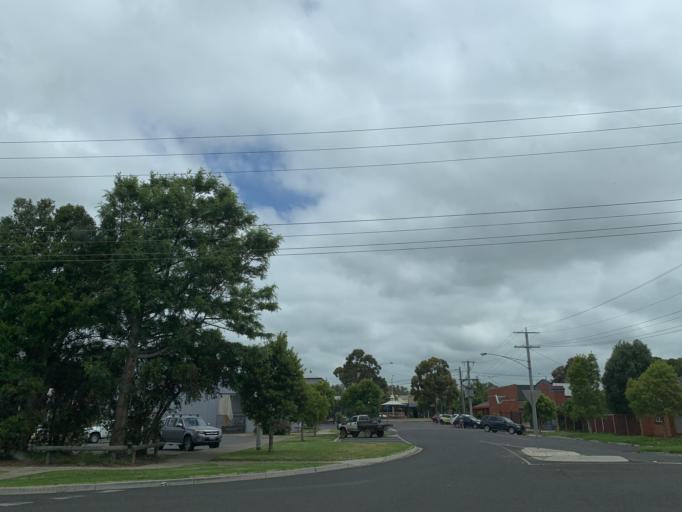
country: AU
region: Victoria
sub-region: Wellington
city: Sale
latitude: -37.9659
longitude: 146.9773
